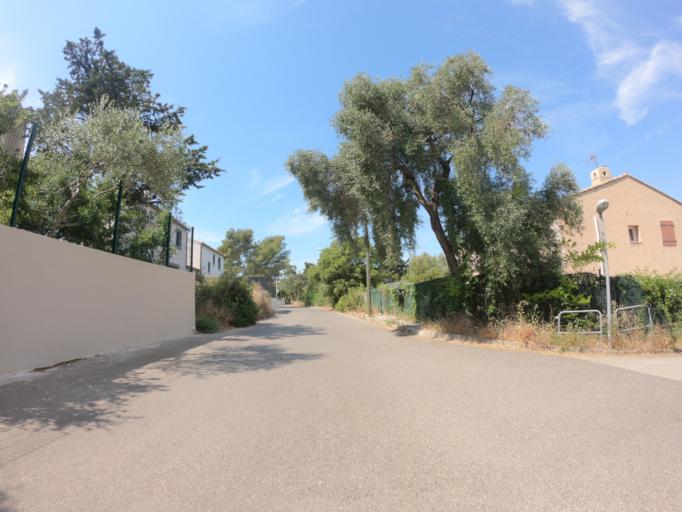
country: FR
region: Provence-Alpes-Cote d'Azur
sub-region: Departement du Var
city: La Valette-du-Var
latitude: 43.1234
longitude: 5.9858
